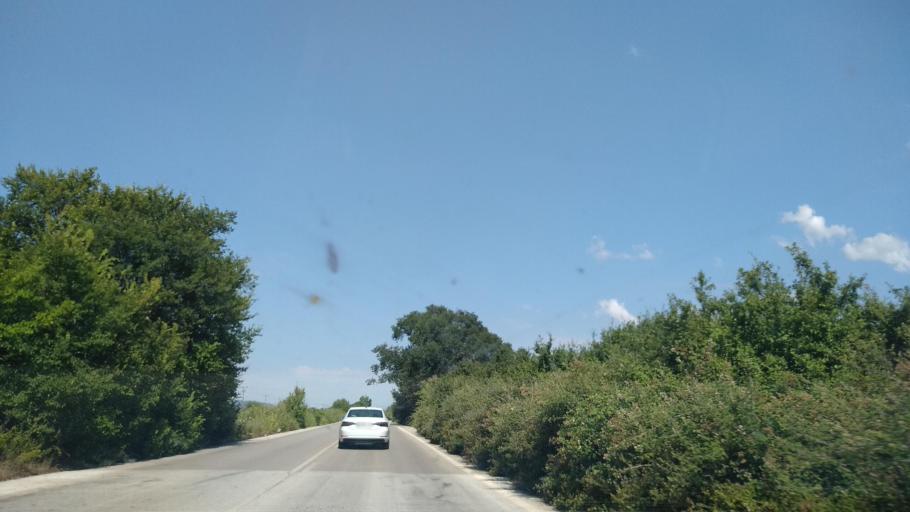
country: GR
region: Central Macedonia
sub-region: Nomos Thessalonikis
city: Nea Apollonia
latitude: 40.6307
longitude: 23.5146
